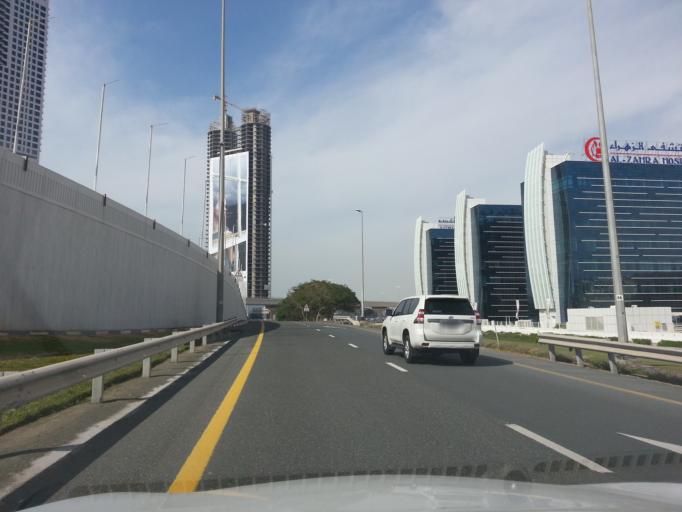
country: AE
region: Dubai
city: Dubai
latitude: 25.1047
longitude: 55.1792
